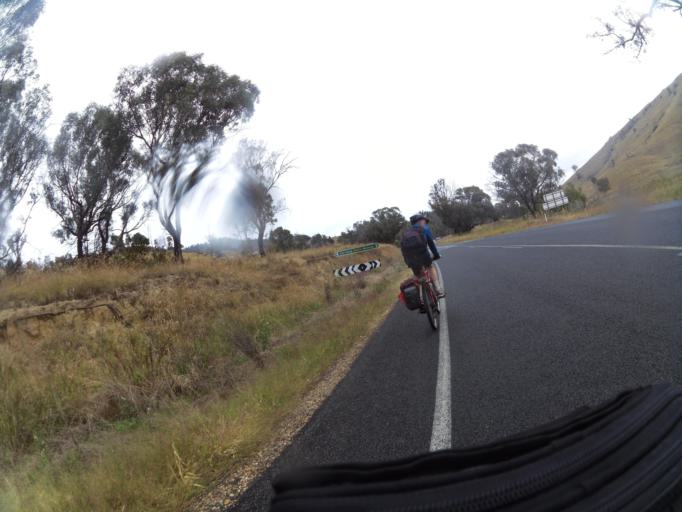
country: AU
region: New South Wales
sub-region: Greater Hume Shire
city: Holbrook
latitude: -36.2215
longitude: 147.7295
